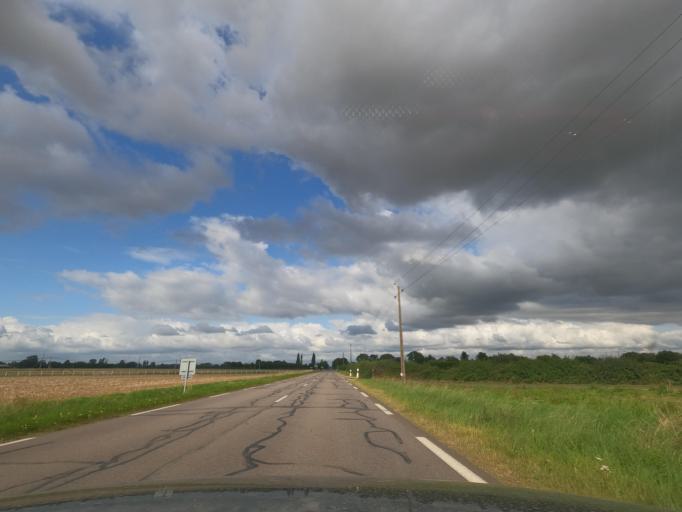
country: FR
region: Lower Normandy
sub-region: Departement du Calvados
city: Orbec
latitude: 48.9459
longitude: 0.4561
